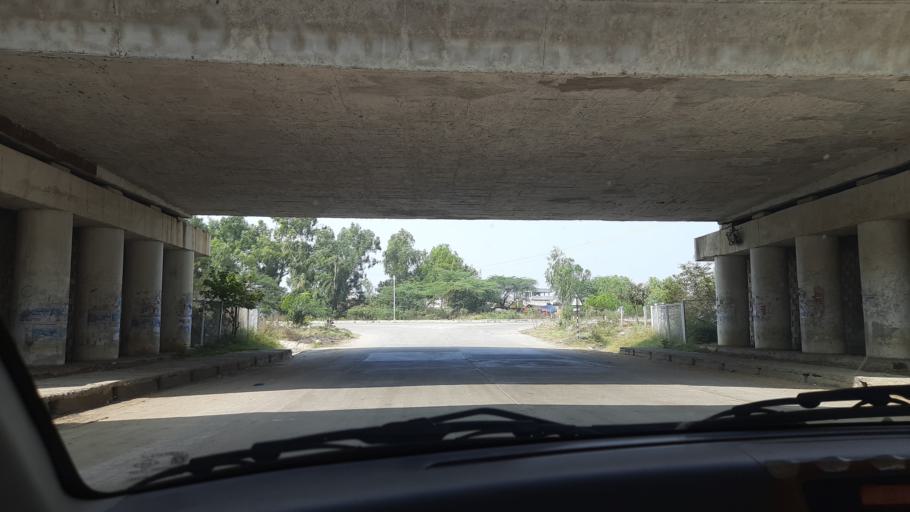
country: IN
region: Telangana
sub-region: Rangareddi
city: Lal Bahadur Nagar
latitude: 17.2813
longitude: 78.6482
